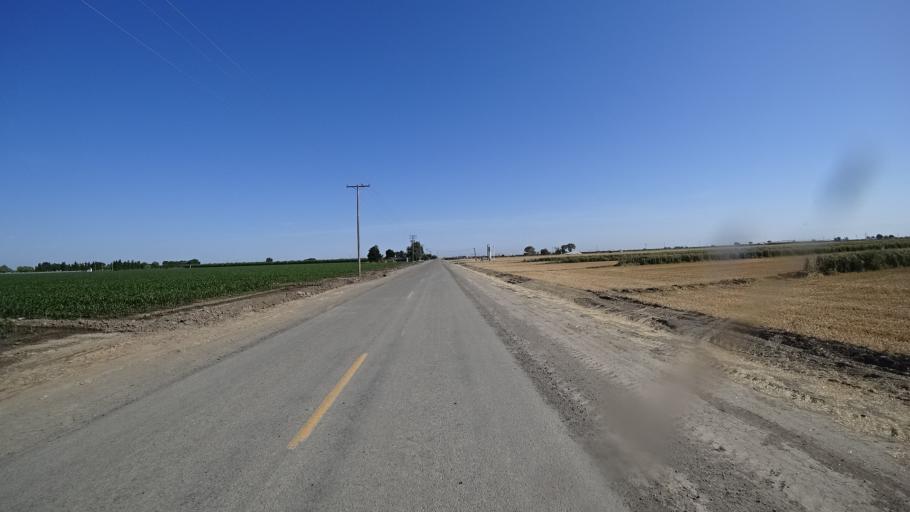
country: US
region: California
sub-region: Kings County
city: Home Garden
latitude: 36.2501
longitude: -119.5563
